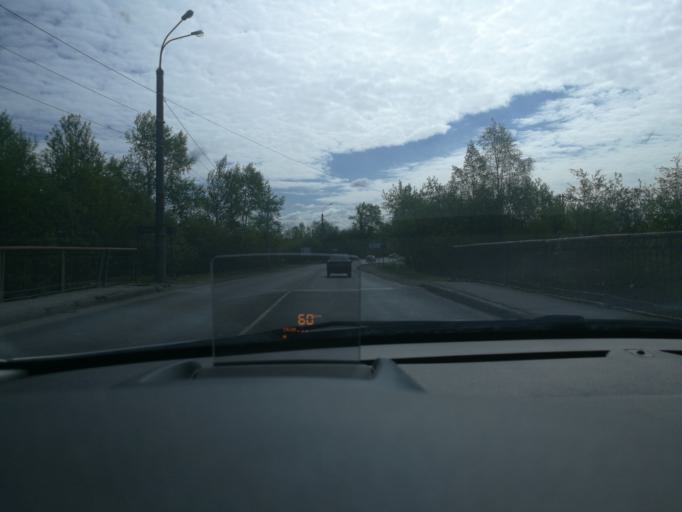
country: RU
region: Arkhangelskaya
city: Arkhangel'sk
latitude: 64.5969
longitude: 40.5428
